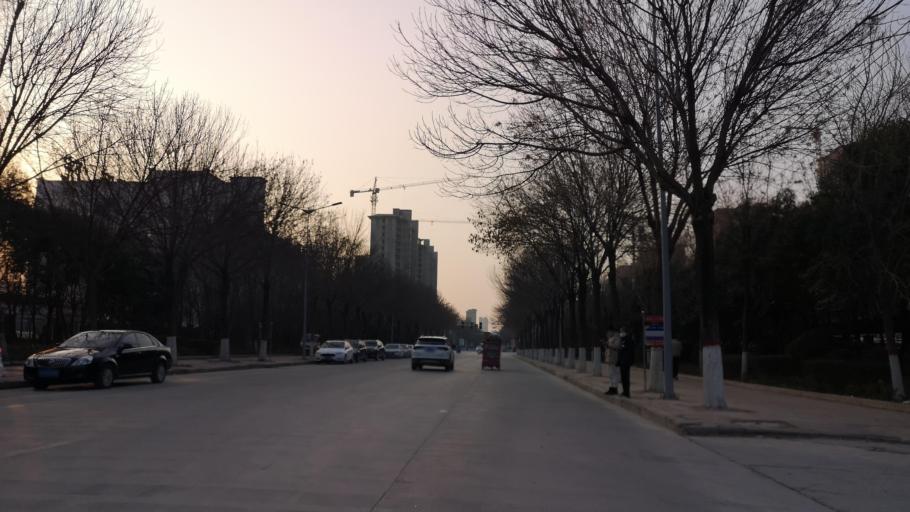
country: CN
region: Henan Sheng
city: Puyang Chengguanzhen
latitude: 35.7237
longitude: 115.0524
